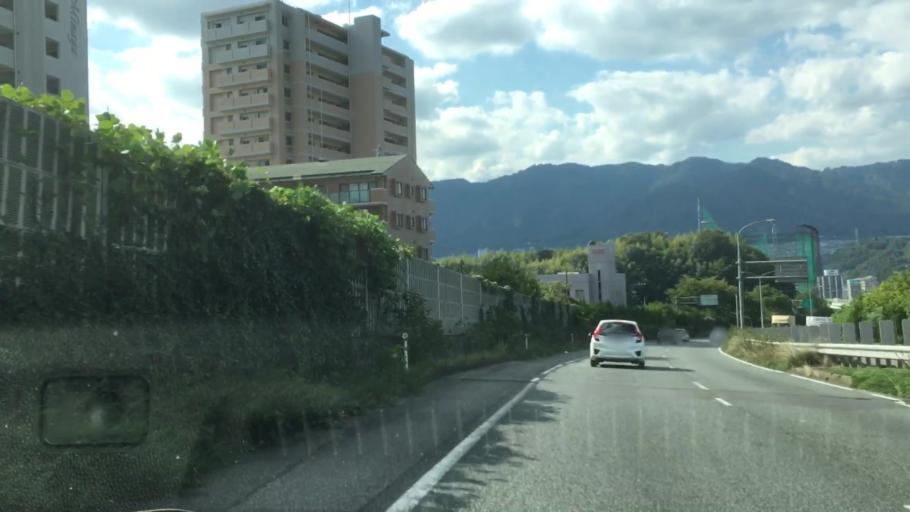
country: JP
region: Hiroshima
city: Hatsukaichi
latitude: 34.3766
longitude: 132.3684
